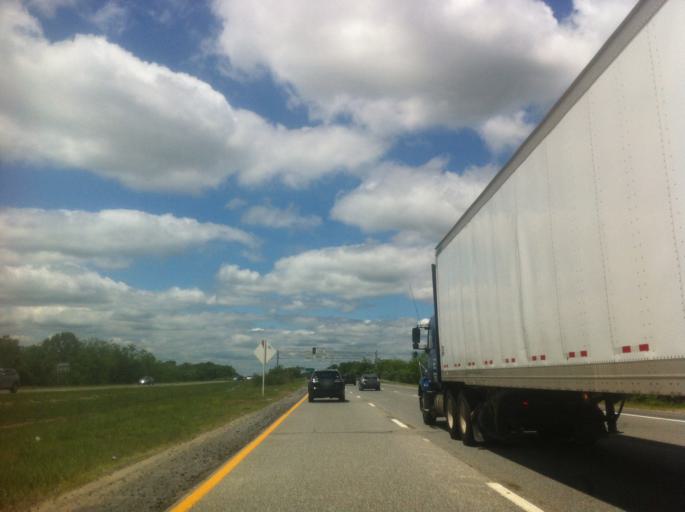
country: US
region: New York
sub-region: Suffolk County
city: Medford
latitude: 40.8237
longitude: -72.9928
